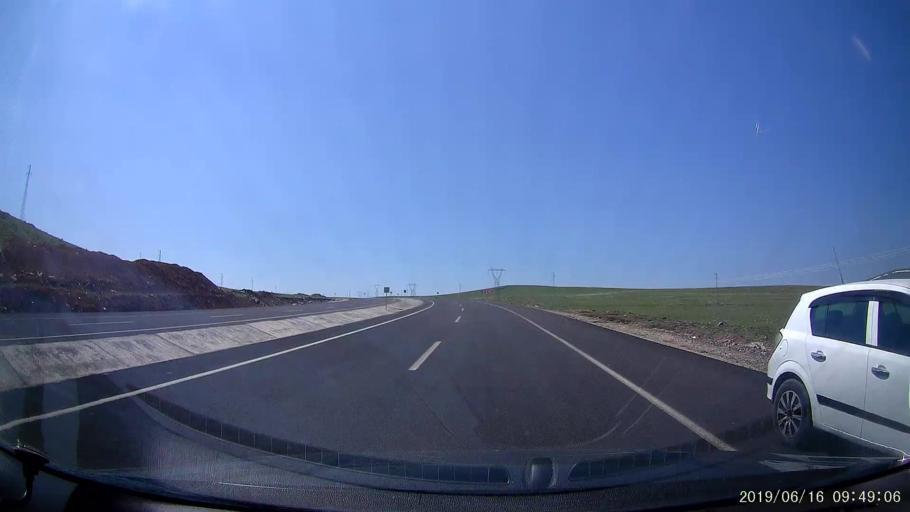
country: TR
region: Kars
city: Digor
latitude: 40.4254
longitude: 43.3563
